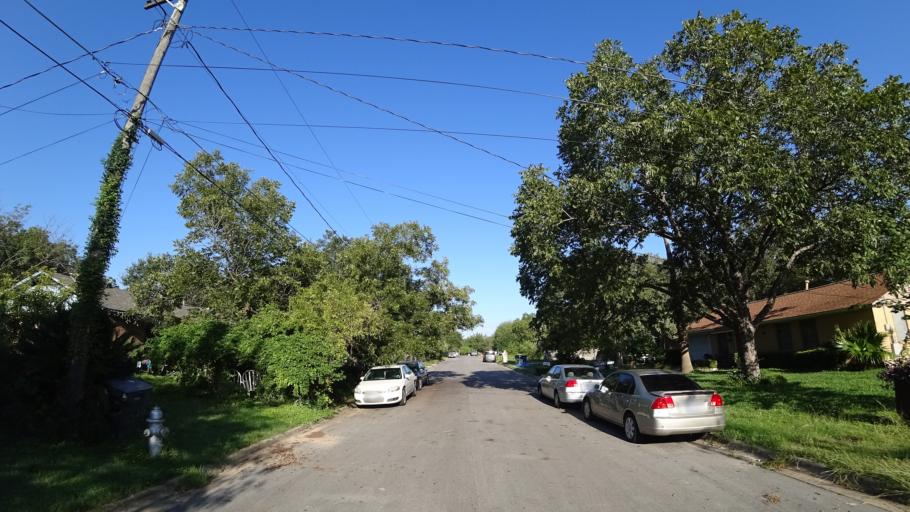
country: US
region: Texas
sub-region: Travis County
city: Austin
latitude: 30.3459
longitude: -97.7017
